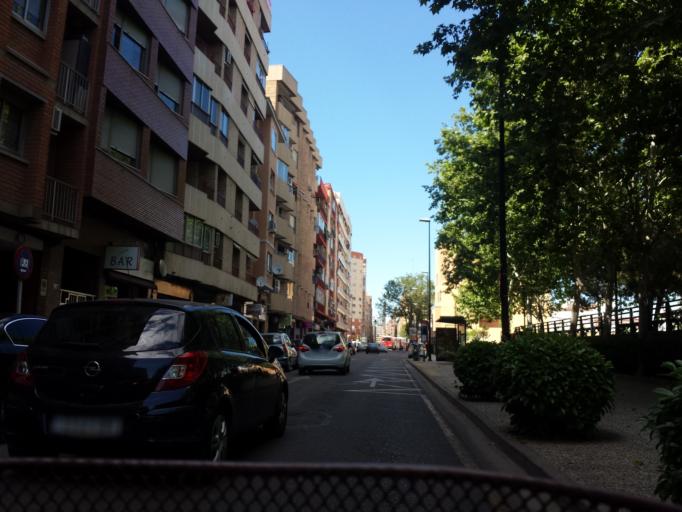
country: ES
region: Aragon
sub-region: Provincia de Zaragoza
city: Zaragoza
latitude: 41.6385
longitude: -0.8741
